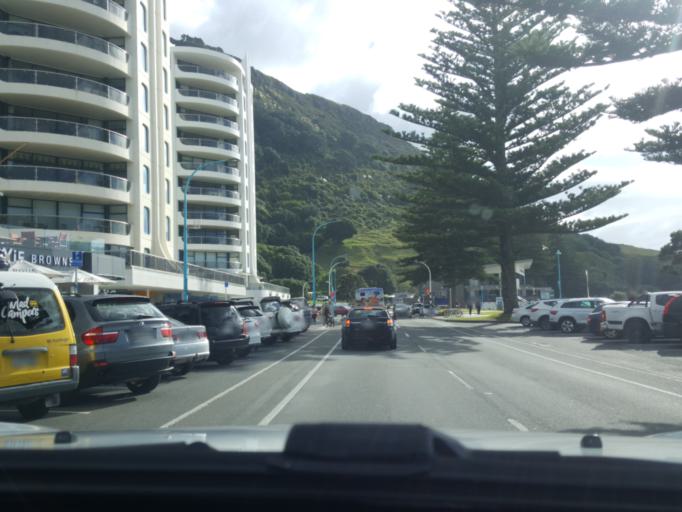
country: NZ
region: Bay of Plenty
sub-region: Tauranga City
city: Tauranga
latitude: -37.6321
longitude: 176.1783
